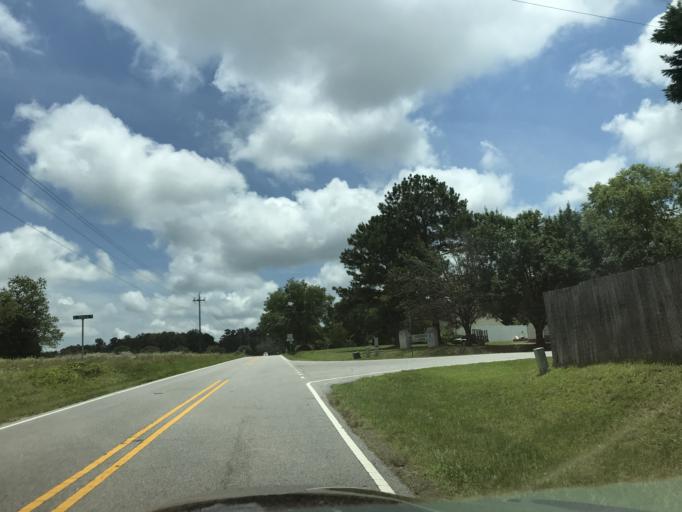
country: US
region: North Carolina
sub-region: Wake County
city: Rolesville
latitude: 35.9565
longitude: -78.3944
